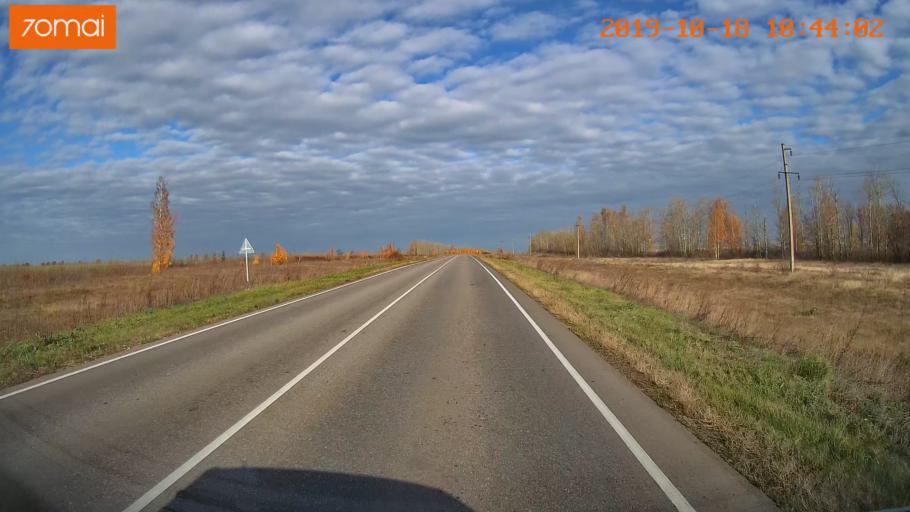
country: RU
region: Tula
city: Yepifan'
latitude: 53.6489
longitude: 38.6829
